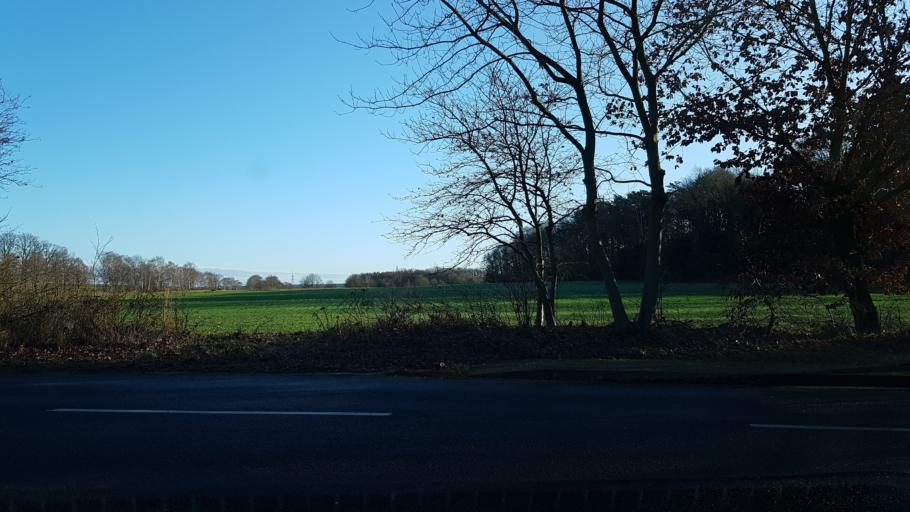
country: DE
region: Lower Saxony
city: Wendisch Evern
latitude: 53.2197
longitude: 10.4698
